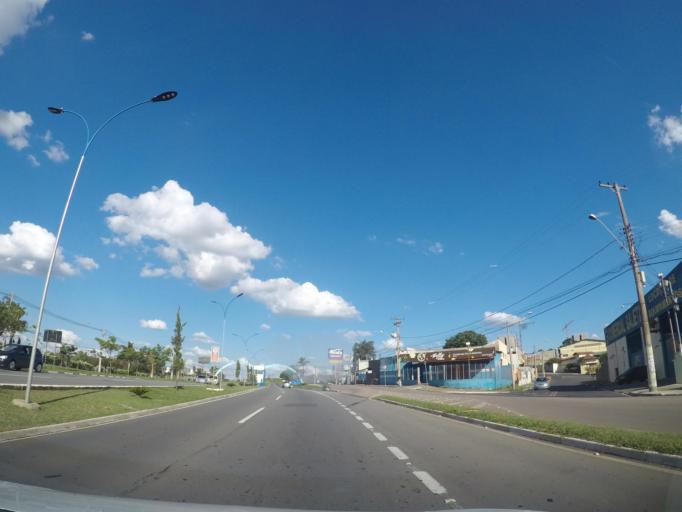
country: BR
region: Sao Paulo
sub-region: Sumare
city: Sumare
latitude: -22.8072
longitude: -47.2514
